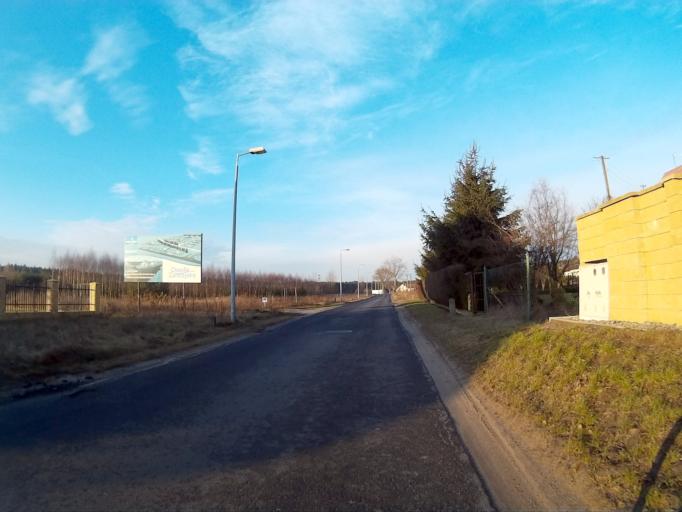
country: PL
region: Kujawsko-Pomorskie
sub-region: Powiat bydgoski
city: Osielsko
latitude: 53.1603
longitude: 18.0799
